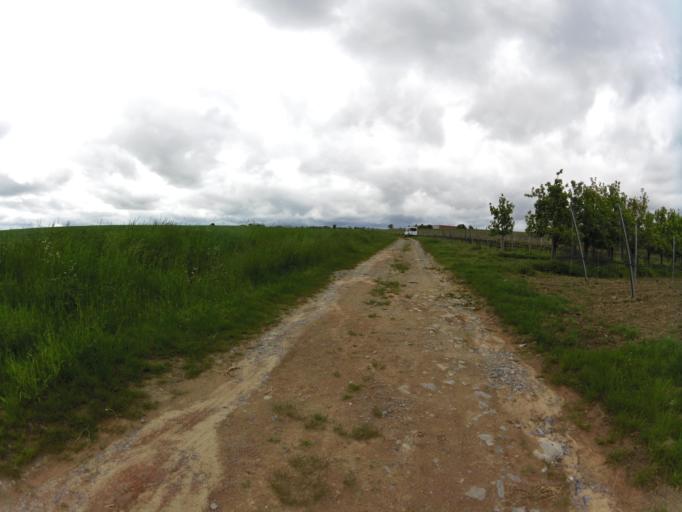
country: DE
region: Bavaria
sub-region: Regierungsbezirk Unterfranken
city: Volkach
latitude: 49.8452
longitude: 10.2211
